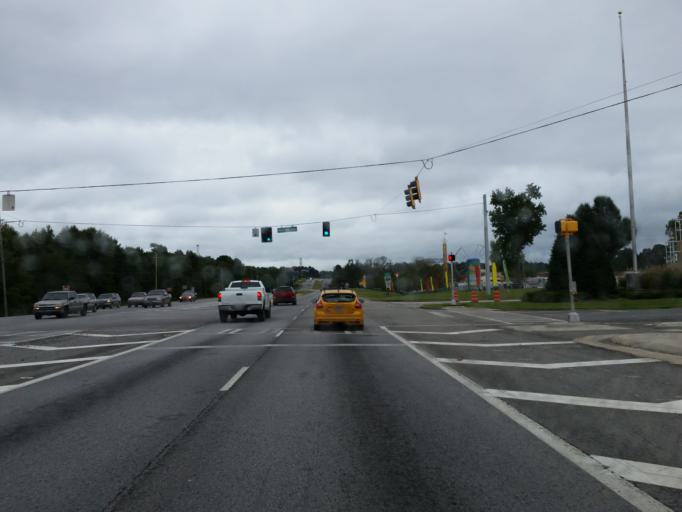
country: US
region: Georgia
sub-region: Henry County
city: Hampton
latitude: 33.3897
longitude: -84.3083
